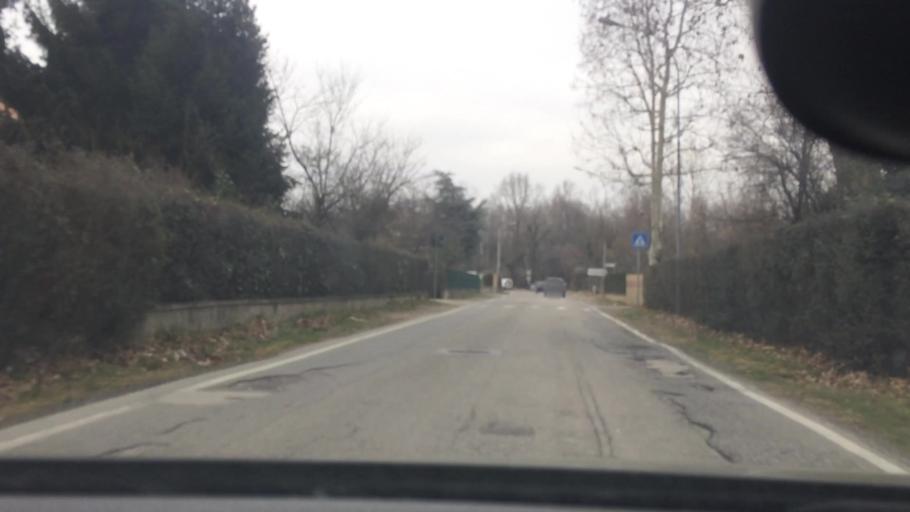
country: IT
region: Lombardy
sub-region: Provincia di Monza e Brianza
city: Villaggio del Sole
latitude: 45.6380
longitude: 9.1093
